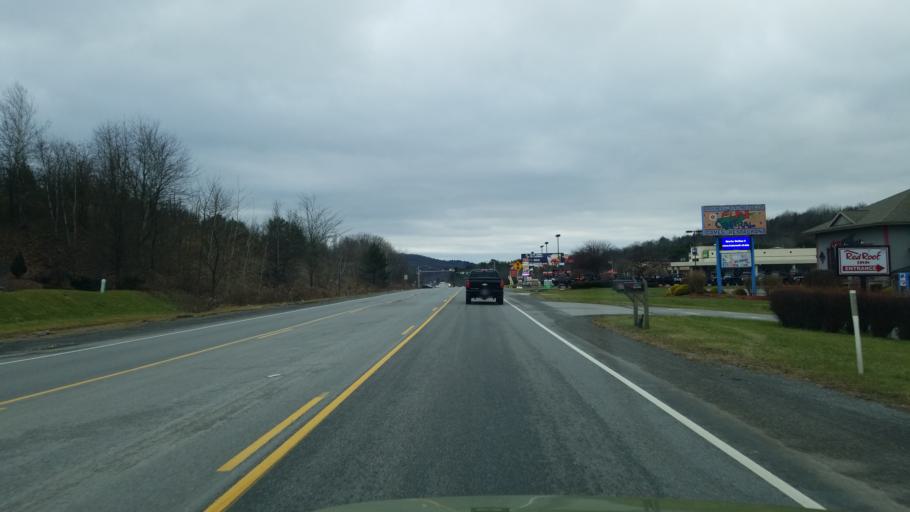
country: US
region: Pennsylvania
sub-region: Clearfield County
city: Clearfield
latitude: 41.0355
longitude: -78.4009
